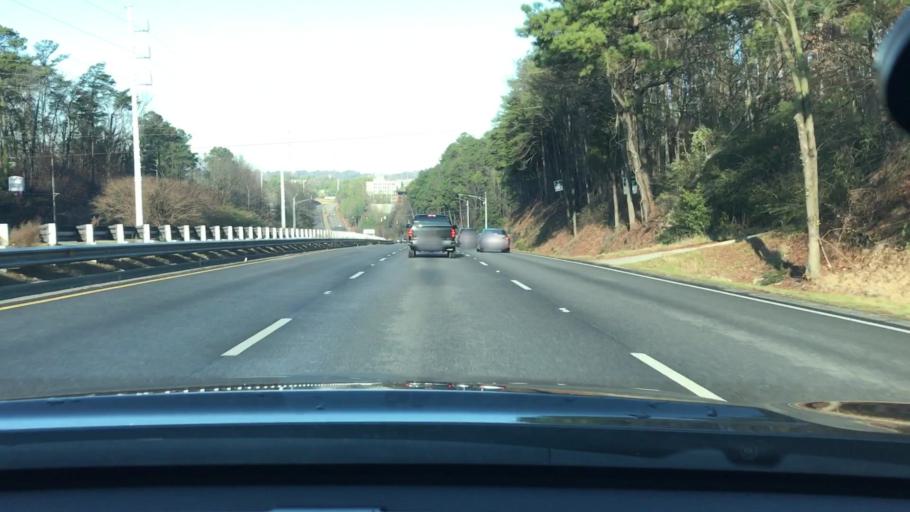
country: US
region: Alabama
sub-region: Jefferson County
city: Cahaba Heights
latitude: 33.4698
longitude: -86.7595
